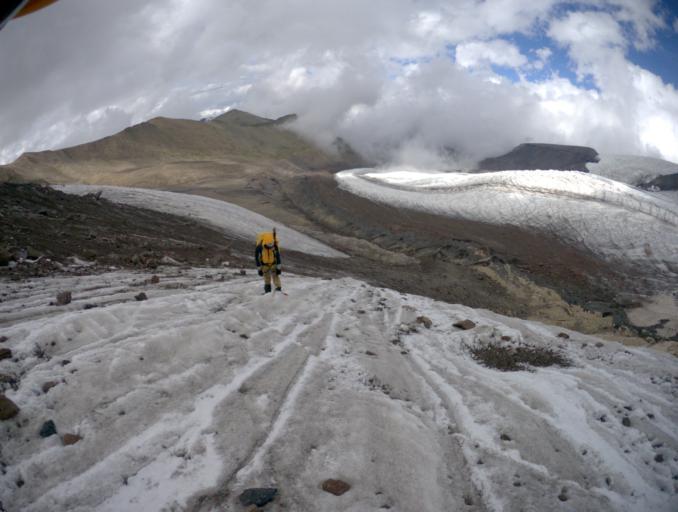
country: RU
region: Kabardino-Balkariya
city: Terskol
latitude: 43.3832
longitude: 42.4164
